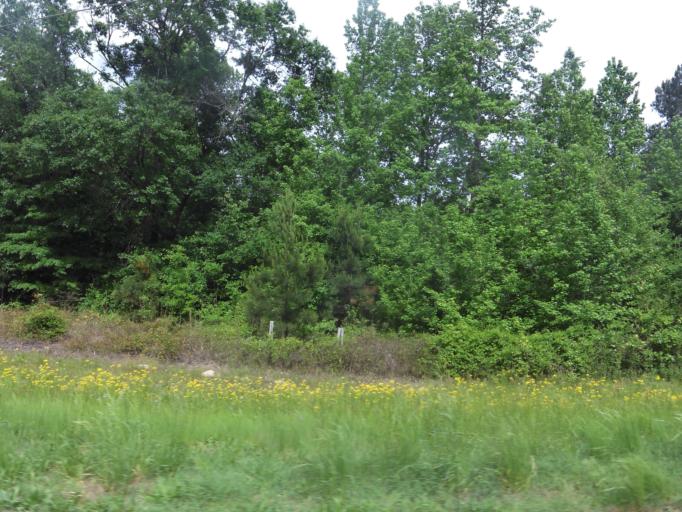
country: US
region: Georgia
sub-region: McDuffie County
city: Thomson
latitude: 33.4372
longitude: -82.4903
